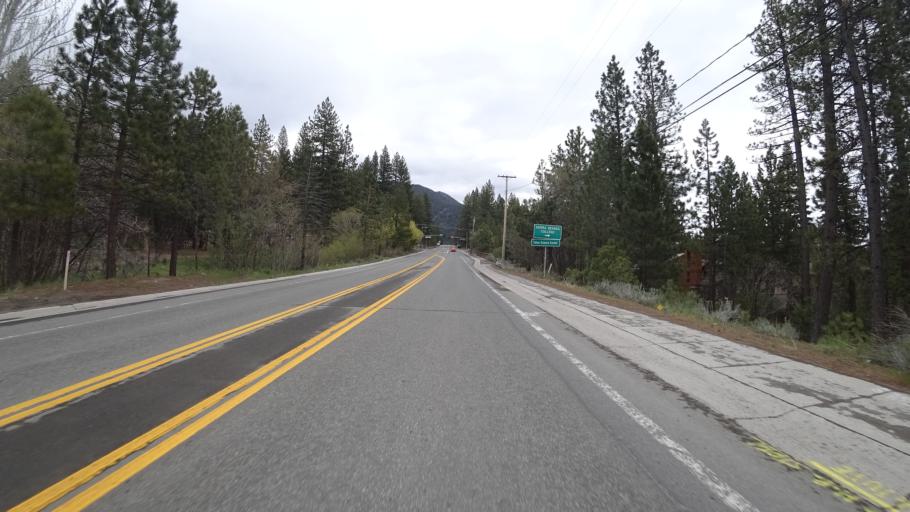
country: US
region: Nevada
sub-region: Washoe County
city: Incline Village
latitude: 39.2460
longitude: -119.9389
